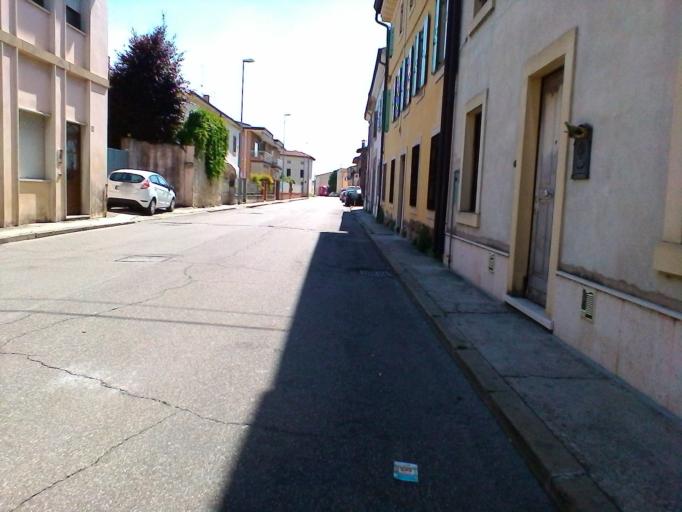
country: IT
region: Veneto
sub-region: Provincia di Verona
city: Povegliano Veronese
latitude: 45.3438
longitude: 10.8822
